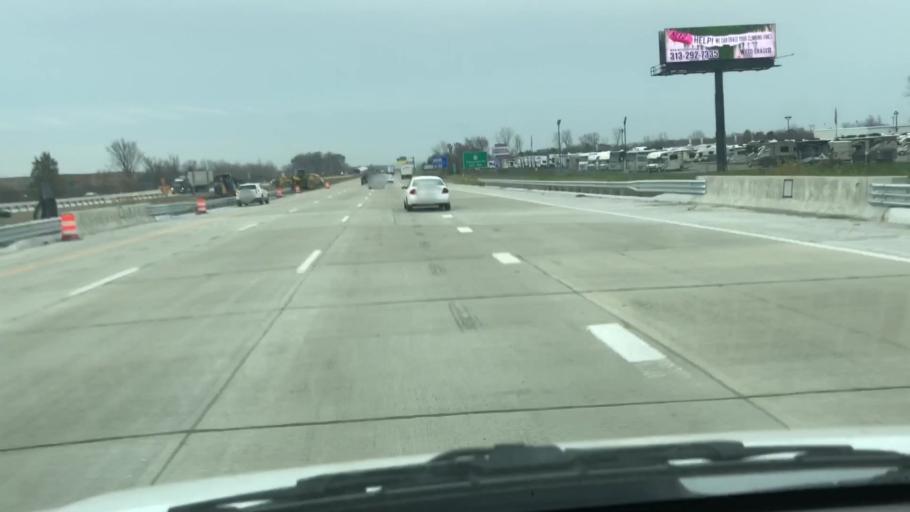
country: US
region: Michigan
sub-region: Wayne County
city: Woodhaven
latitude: 42.1829
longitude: -83.2440
